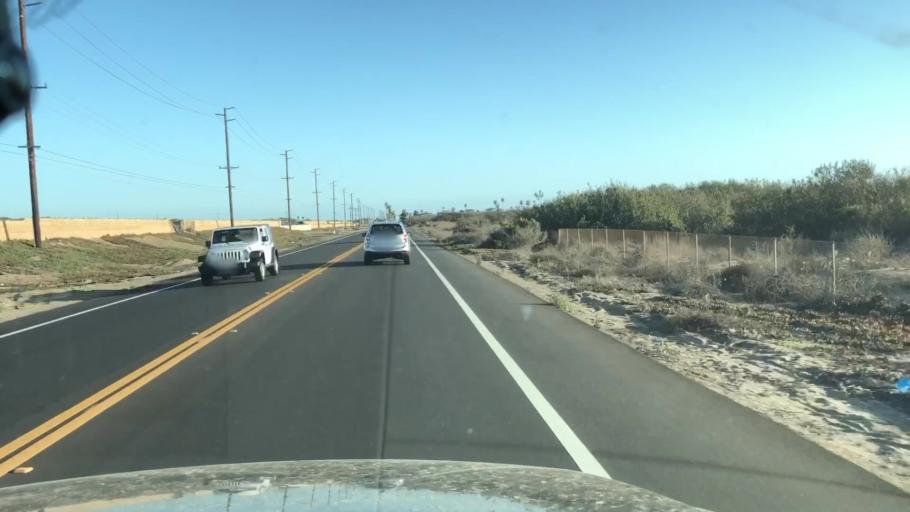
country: US
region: California
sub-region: Ventura County
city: Oxnard Shores
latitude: 34.2026
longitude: -119.2452
